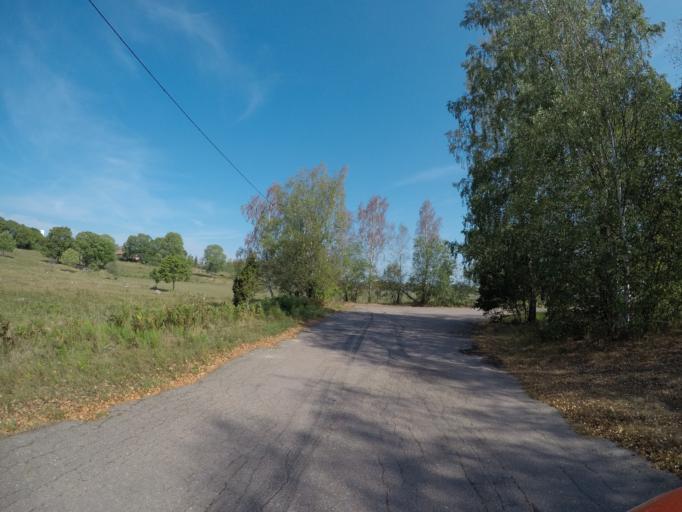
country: AX
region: Alands landsbygd
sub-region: Finstroem
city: Finstroem
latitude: 60.2330
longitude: 19.9959
